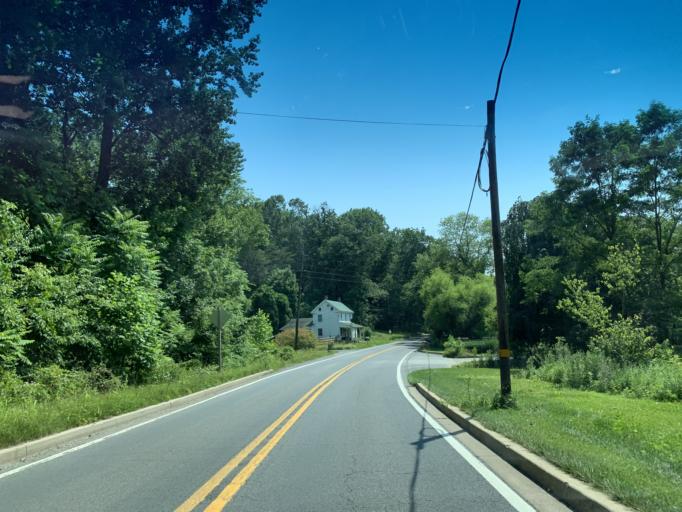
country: US
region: Maryland
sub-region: Frederick County
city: Urbana
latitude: 39.2684
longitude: -77.3403
